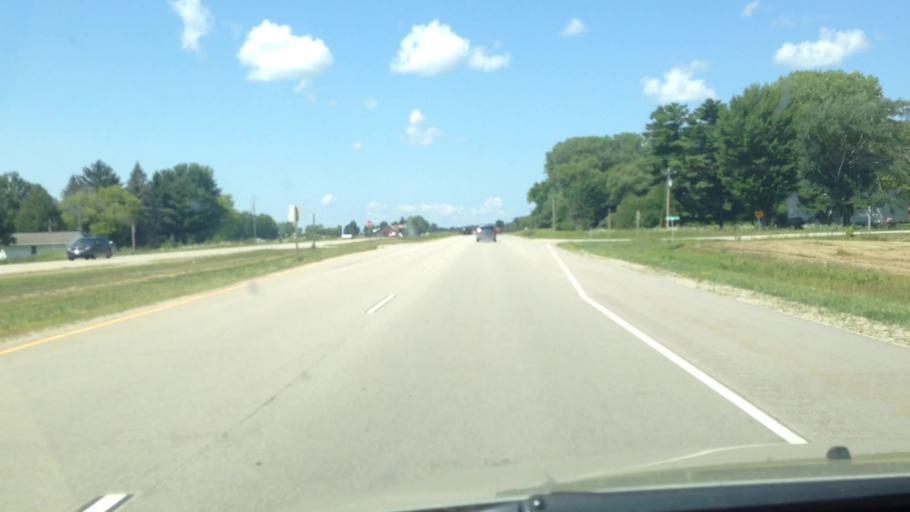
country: US
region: Wisconsin
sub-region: Oconto County
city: Oconto Falls
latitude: 44.8007
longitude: -88.0052
